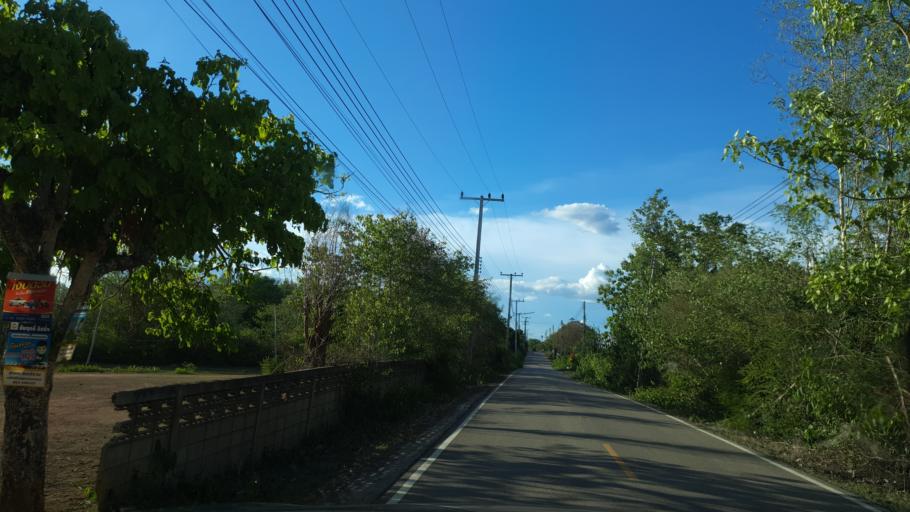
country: TH
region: Lampang
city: Sop Prap
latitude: 17.8826
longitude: 99.3115
